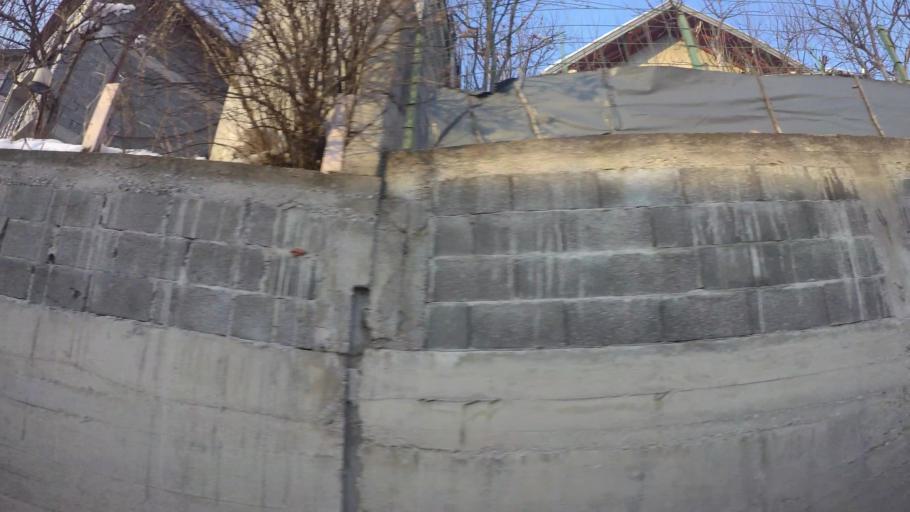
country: BA
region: Federation of Bosnia and Herzegovina
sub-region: Kanton Sarajevo
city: Sarajevo
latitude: 43.8389
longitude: 18.3564
